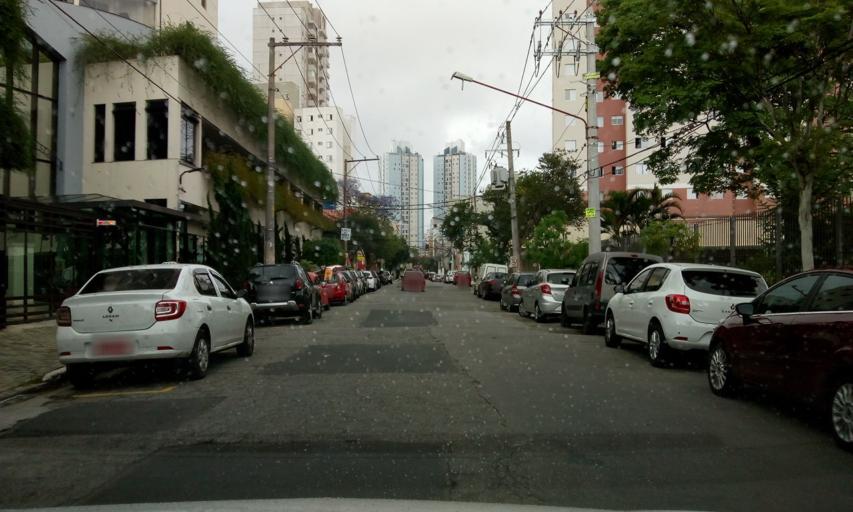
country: BR
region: Sao Paulo
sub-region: Sao Paulo
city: Sao Paulo
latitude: -23.5587
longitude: -46.6229
